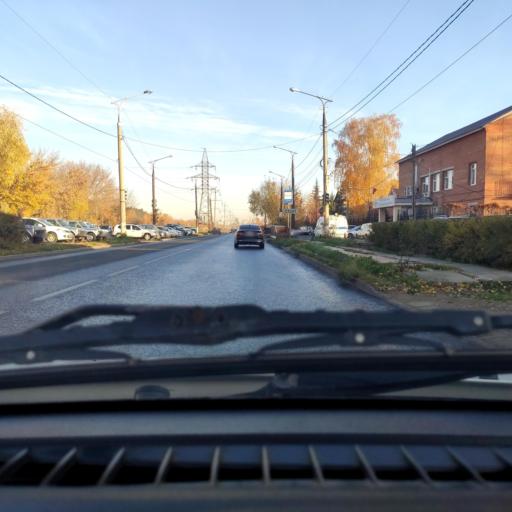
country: RU
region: Samara
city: Tol'yatti
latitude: 53.5127
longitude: 49.3954
